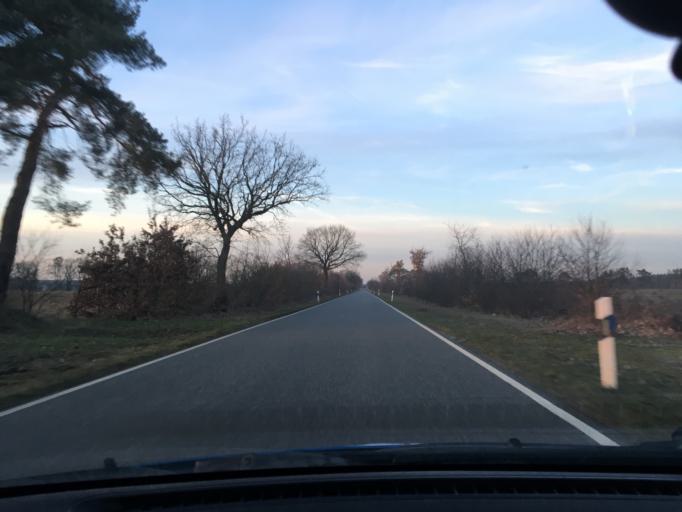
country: DE
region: Schleswig-Holstein
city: Langenlehsten
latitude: 53.5190
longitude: 10.7451
